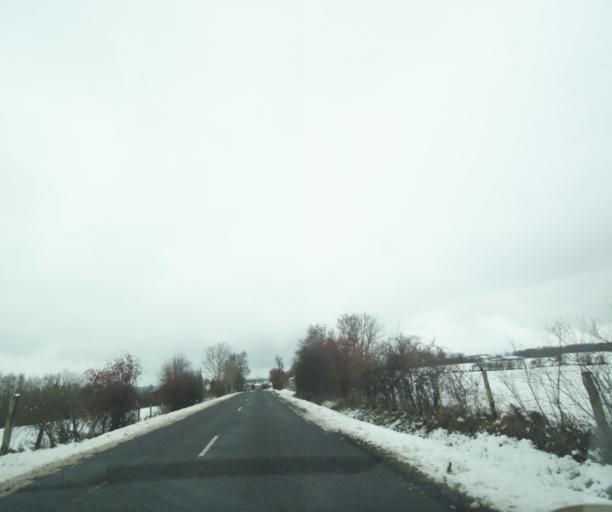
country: FR
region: Champagne-Ardenne
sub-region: Departement de la Haute-Marne
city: Laneuville-a-Remy
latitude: 48.4131
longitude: 4.8332
